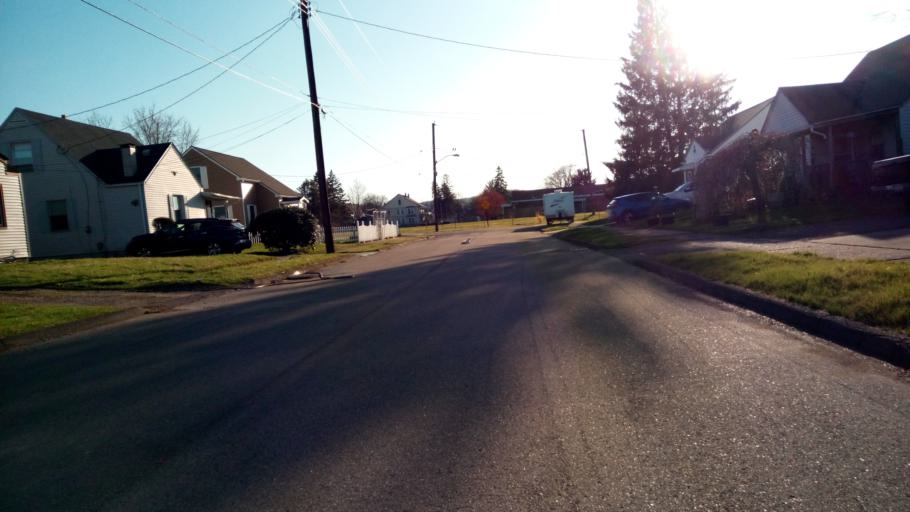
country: US
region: New York
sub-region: Chemung County
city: Elmira
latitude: 42.0786
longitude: -76.7857
